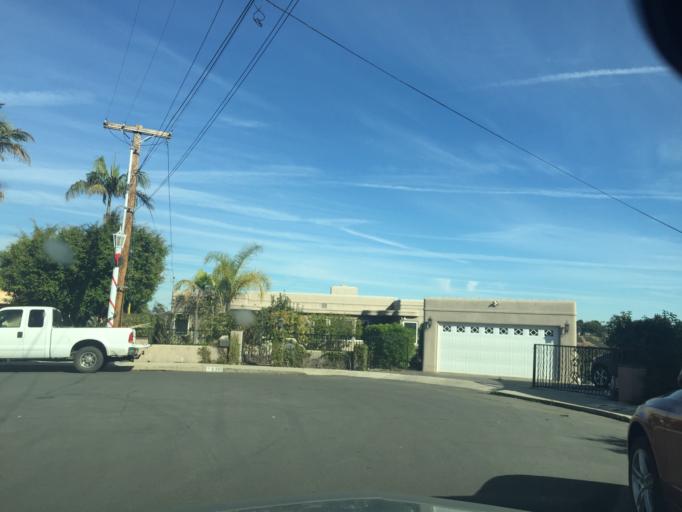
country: US
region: California
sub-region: San Diego County
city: Lemon Grove
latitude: 32.7730
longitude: -117.1000
